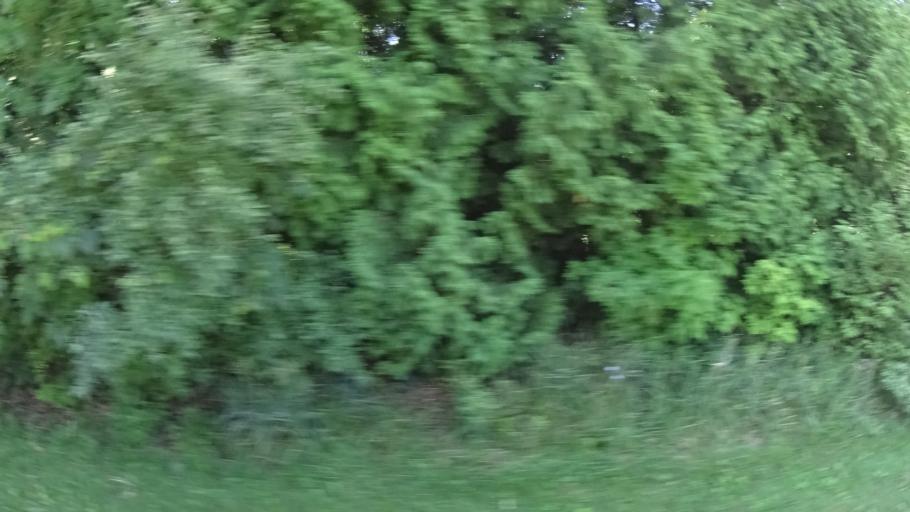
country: US
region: Indiana
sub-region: Madison County
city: Ingalls
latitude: 39.9592
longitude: -85.8313
